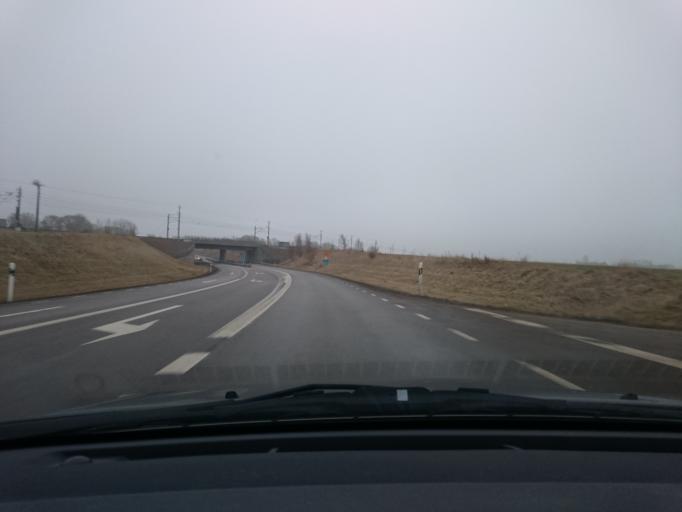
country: SE
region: Skane
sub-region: Bastads Kommun
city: Forslov
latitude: 56.3359
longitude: 12.8045
